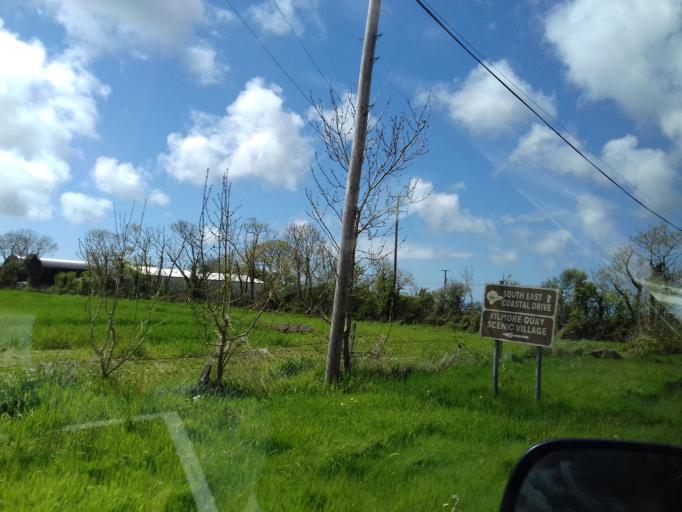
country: IE
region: Leinster
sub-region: Loch Garman
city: Loch Garman
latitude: 52.2846
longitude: -6.6321
